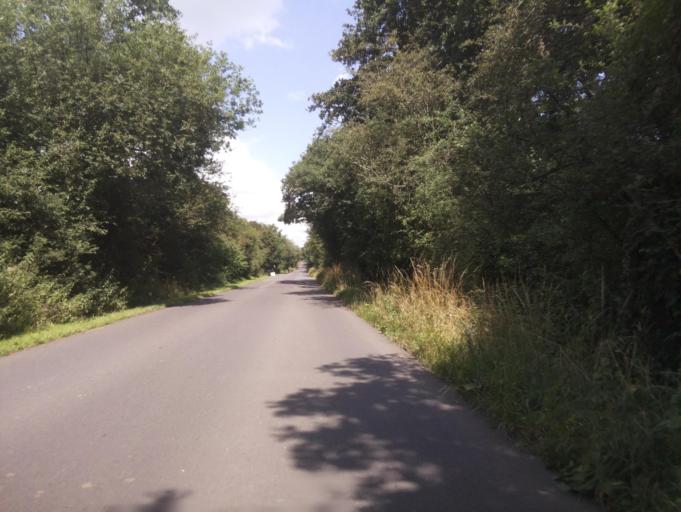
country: GB
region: England
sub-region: Wiltshire
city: Minety
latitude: 51.5957
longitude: -1.9372
